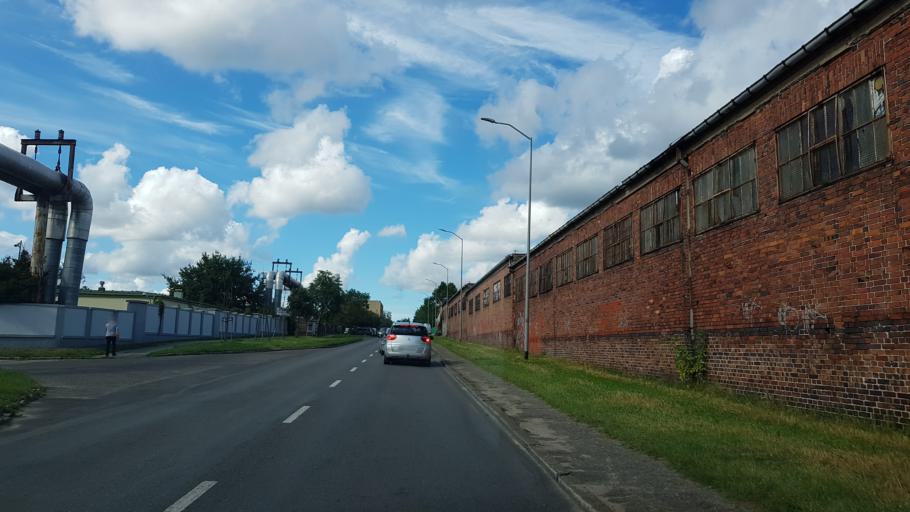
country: PL
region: West Pomeranian Voivodeship
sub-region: Szczecin
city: Szczecin
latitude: 53.4472
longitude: 14.4973
